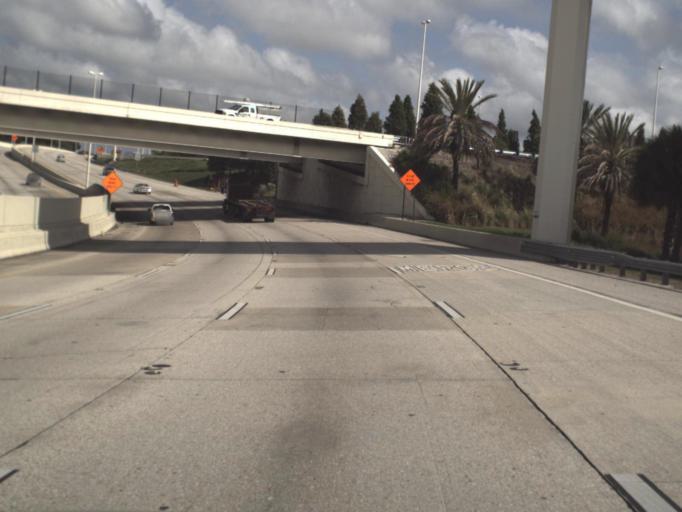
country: US
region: Florida
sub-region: Hillsborough County
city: Tampa
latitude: 27.9640
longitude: -82.4524
